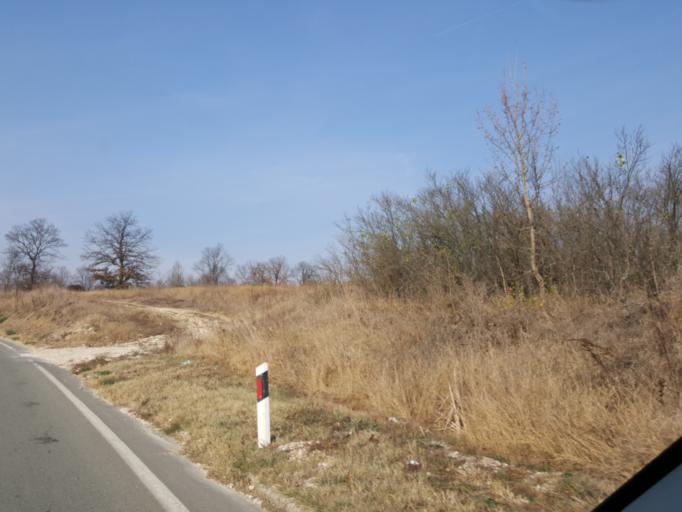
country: RS
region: Central Serbia
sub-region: Borski Okrug
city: Bor
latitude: 43.9319
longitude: 22.0926
